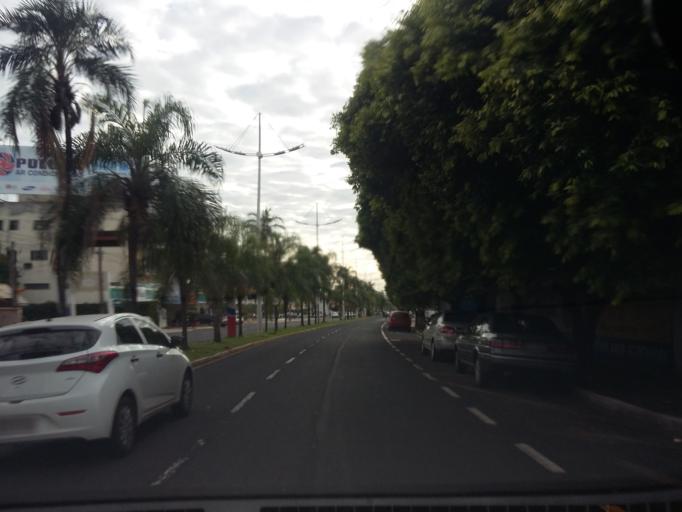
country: BR
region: Sao Paulo
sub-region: Sao Jose Do Rio Preto
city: Sao Jose do Rio Preto
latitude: -20.8327
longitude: -49.3993
